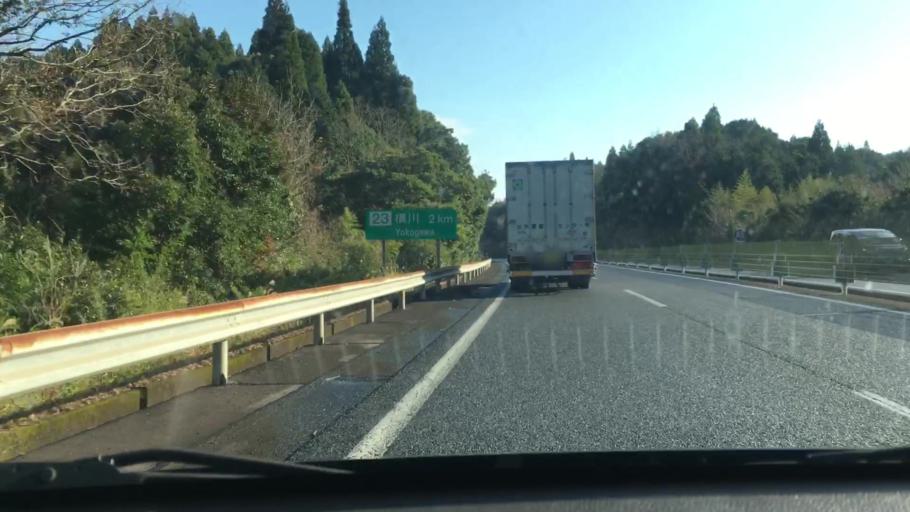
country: JP
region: Kagoshima
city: Okuchi-shinohara
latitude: 31.9139
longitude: 130.7037
